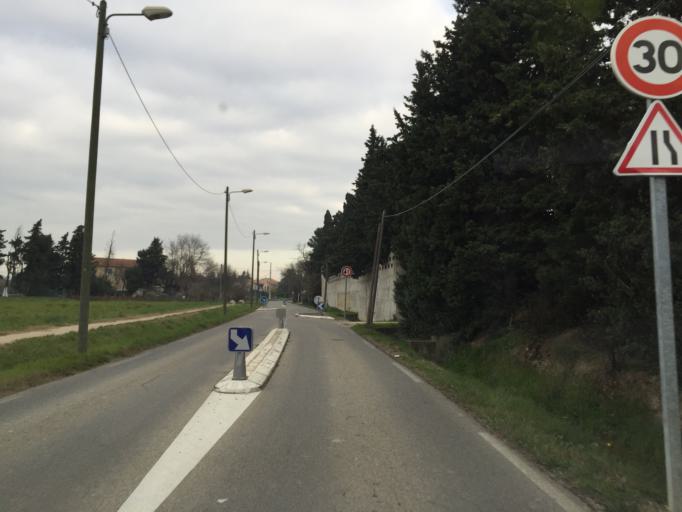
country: FR
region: Provence-Alpes-Cote d'Azur
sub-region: Departement du Vaucluse
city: Sorgues
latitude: 44.0114
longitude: 4.8661
